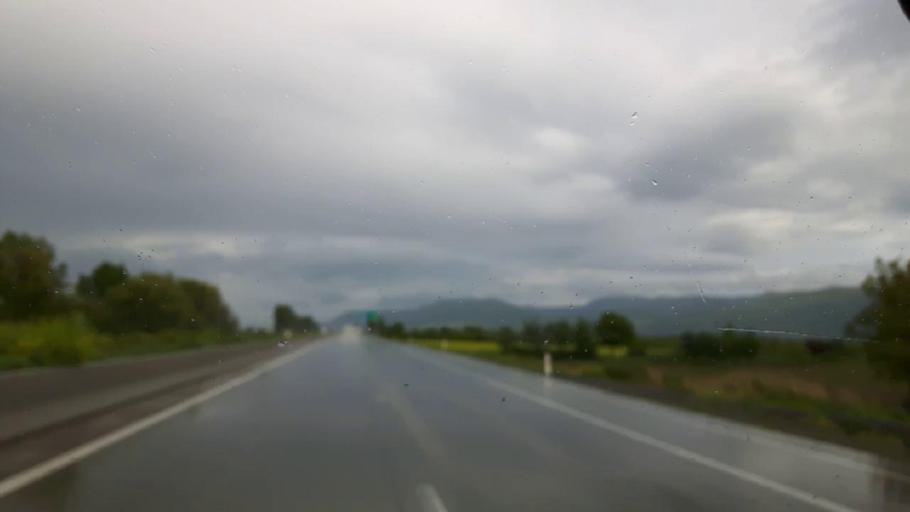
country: GE
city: Agara
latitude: 42.0390
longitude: 43.9333
